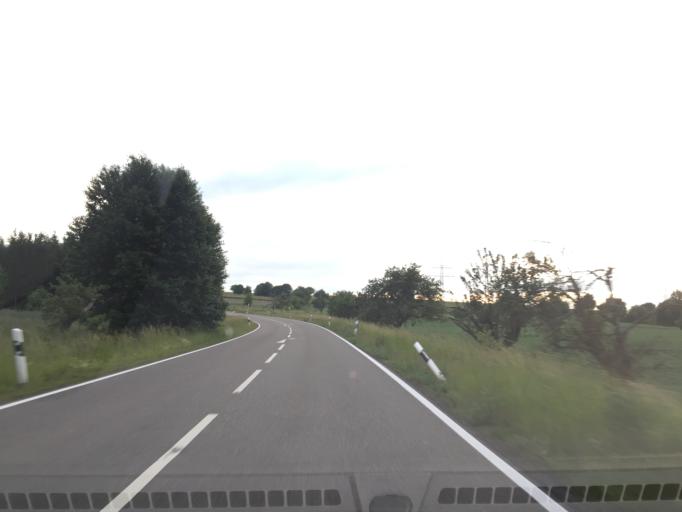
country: DE
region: Rheinland-Pfalz
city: Weroth
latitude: 50.4548
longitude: 7.9523
